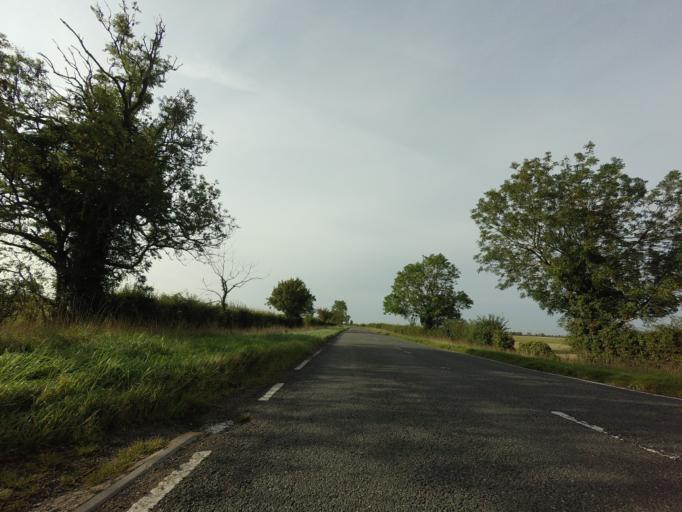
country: GB
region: England
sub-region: Cambridgeshire
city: Harston
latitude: 52.1074
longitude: 0.0875
